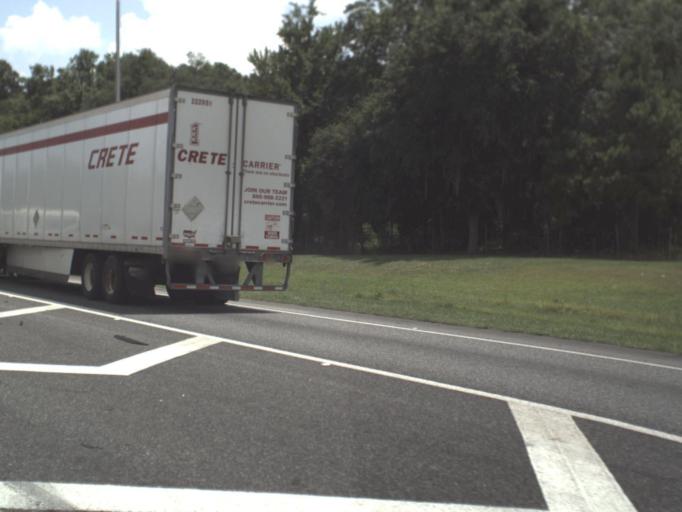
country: US
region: Florida
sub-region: Hamilton County
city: Jasper
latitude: 30.4295
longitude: -82.9089
